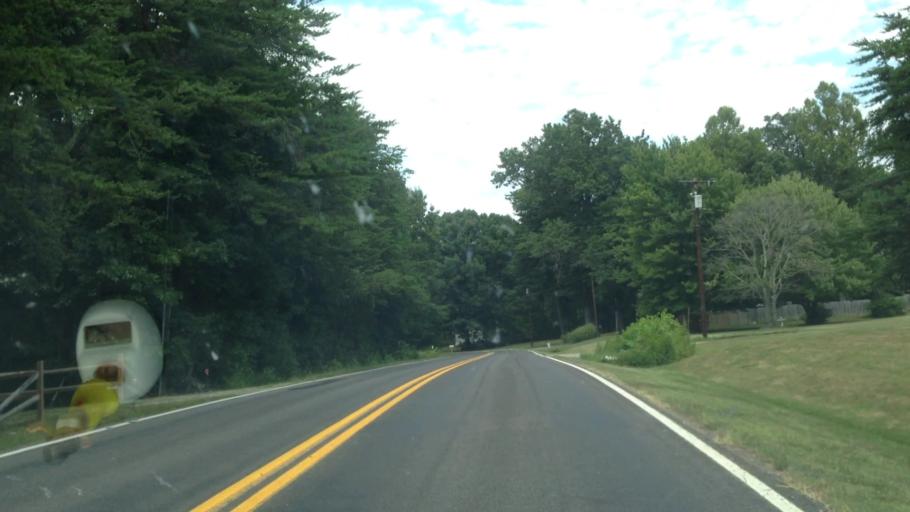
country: US
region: North Carolina
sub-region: Stokes County
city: Walnut Cove
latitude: 36.2556
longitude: -80.0976
